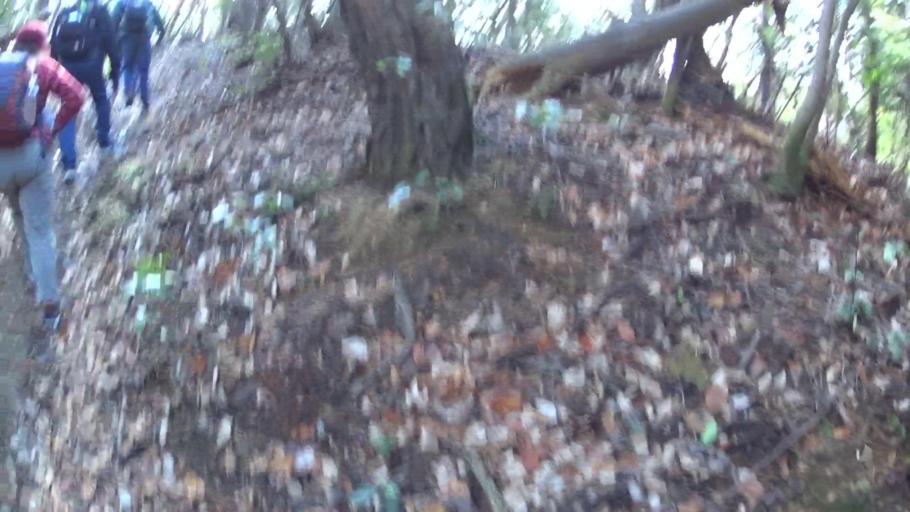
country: JP
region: Kyoto
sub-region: Kyoto-shi
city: Kamigyo-ku
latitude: 35.0982
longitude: 135.7575
